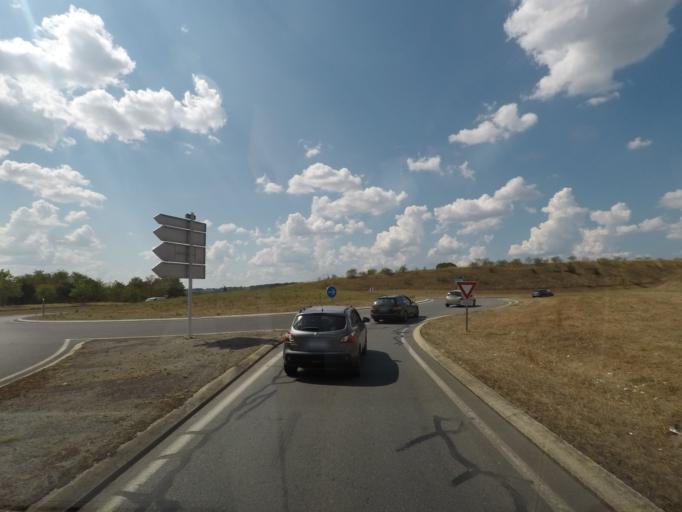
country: FR
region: Midi-Pyrenees
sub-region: Departement du Lot
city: Le Vigan
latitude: 44.6985
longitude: 1.5858
